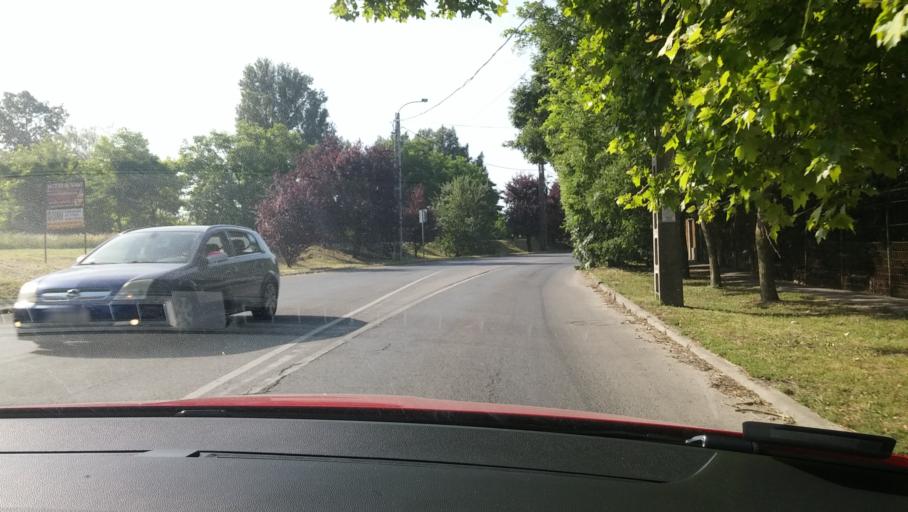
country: HU
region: Pest
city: Rackeve
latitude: 47.1715
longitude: 18.9441
